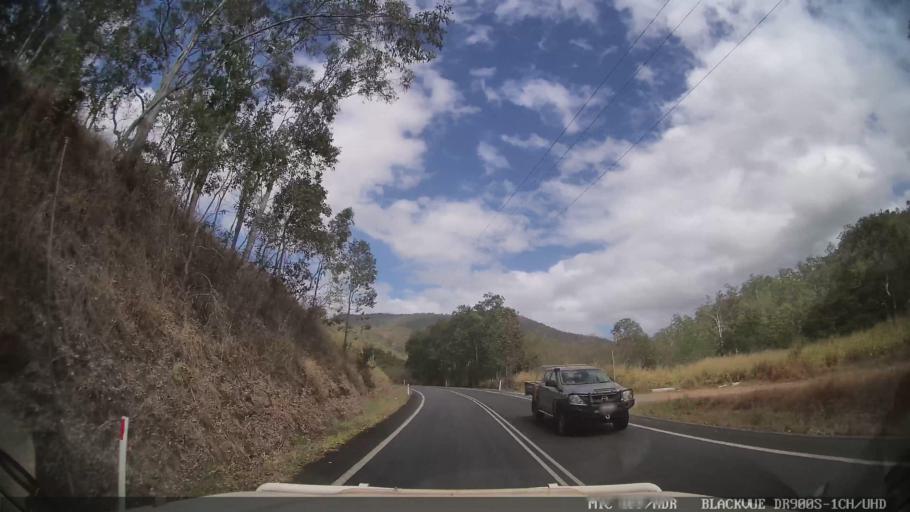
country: AU
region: Queensland
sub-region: Cairns
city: Woree
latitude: -17.1468
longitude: 145.7141
